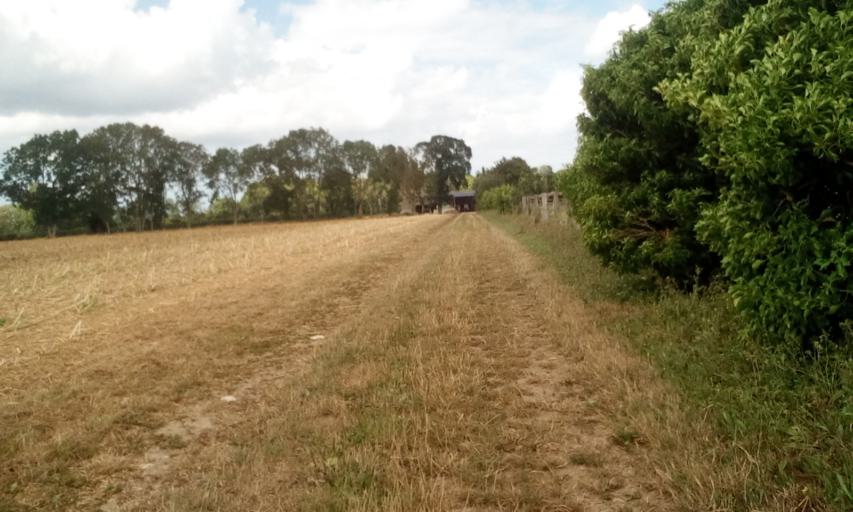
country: FR
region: Lower Normandy
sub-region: Departement du Calvados
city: Creully
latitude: 49.3094
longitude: -0.5546
